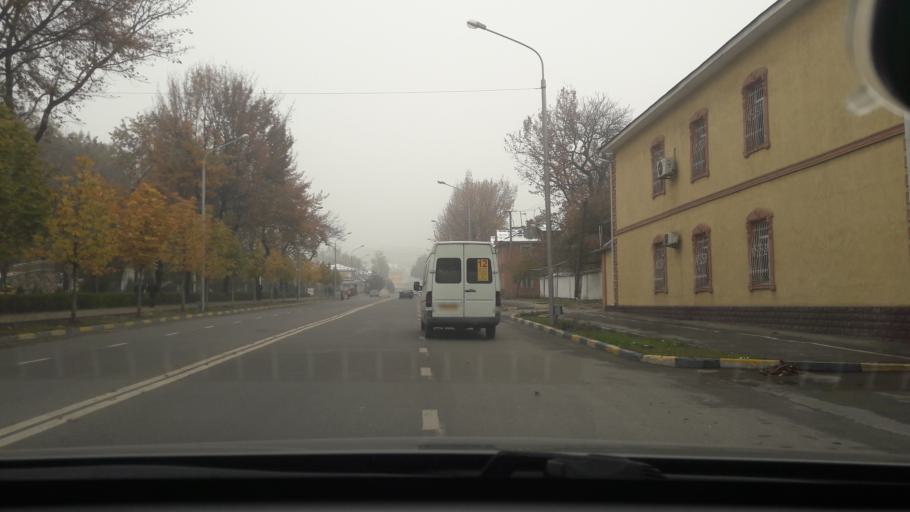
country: TJ
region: Dushanbe
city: Dushanbe
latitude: 38.5787
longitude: 68.7957
